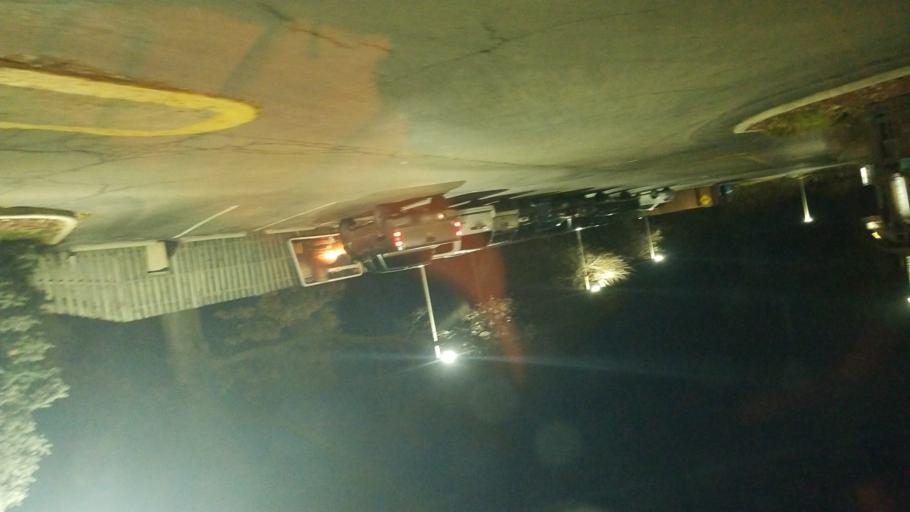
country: US
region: Indiana
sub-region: Adams County
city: Berne
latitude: 40.6640
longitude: -84.9558
